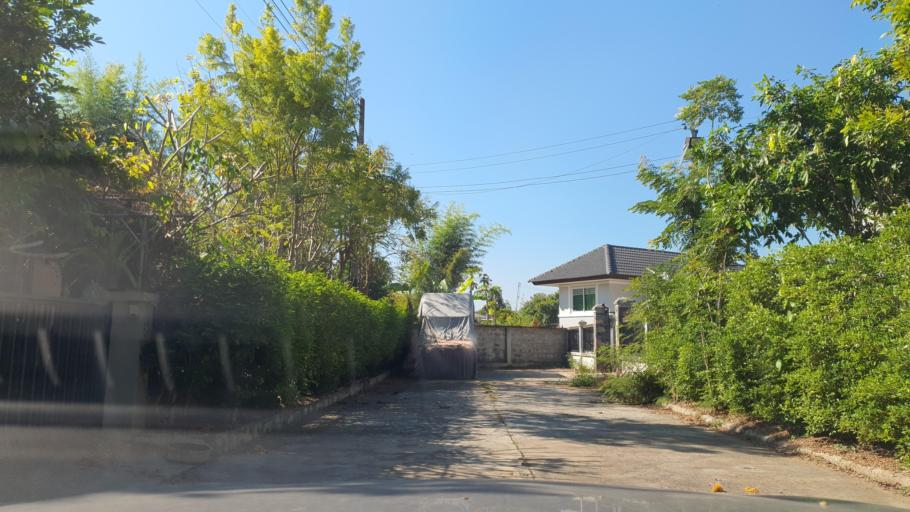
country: TH
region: Chiang Mai
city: Hang Dong
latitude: 18.6956
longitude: 98.9350
